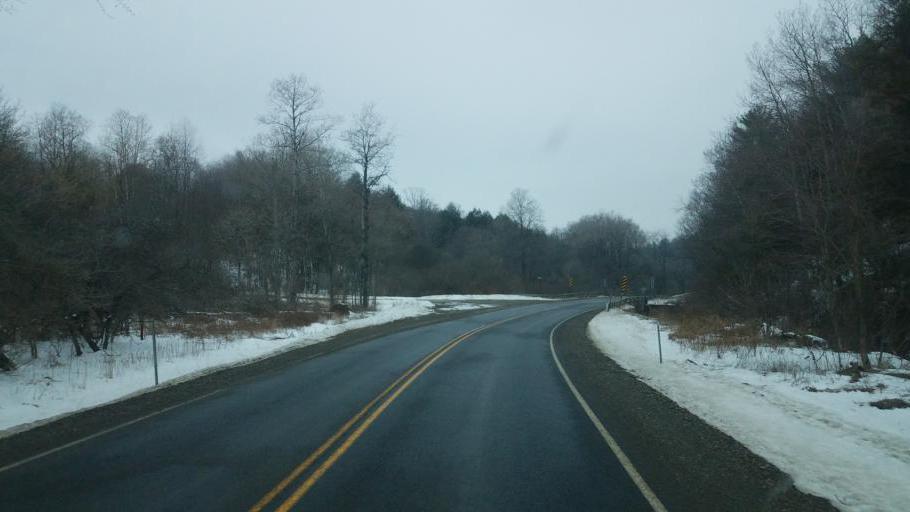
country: US
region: New York
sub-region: Allegany County
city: Andover
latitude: 42.0286
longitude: -77.7420
